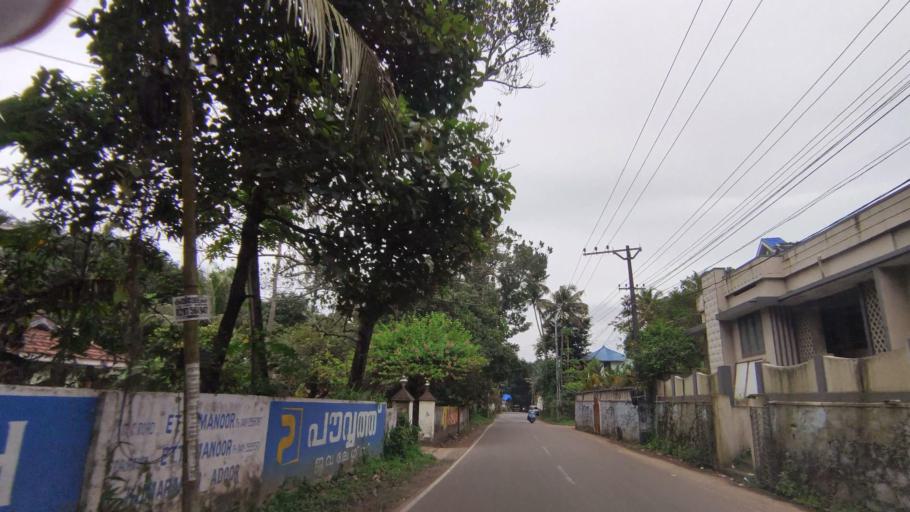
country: IN
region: Kerala
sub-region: Kottayam
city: Kottayam
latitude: 9.6556
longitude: 76.5258
